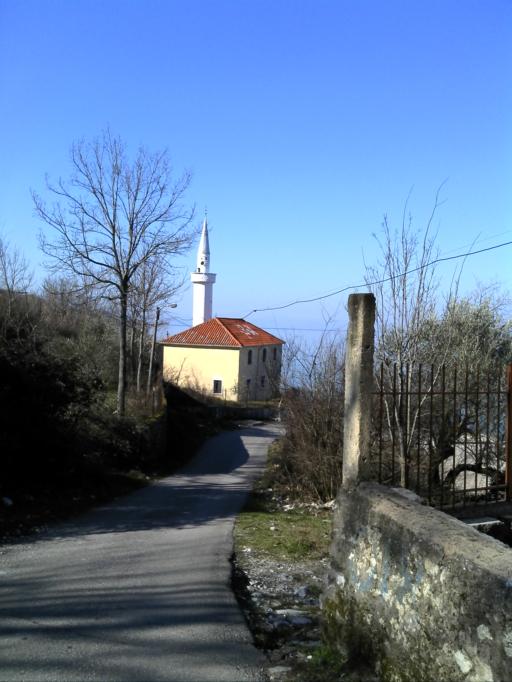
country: AL
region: Shkoder
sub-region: Rrethi i Shkodres
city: Dajc
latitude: 42.0717
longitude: 19.3983
